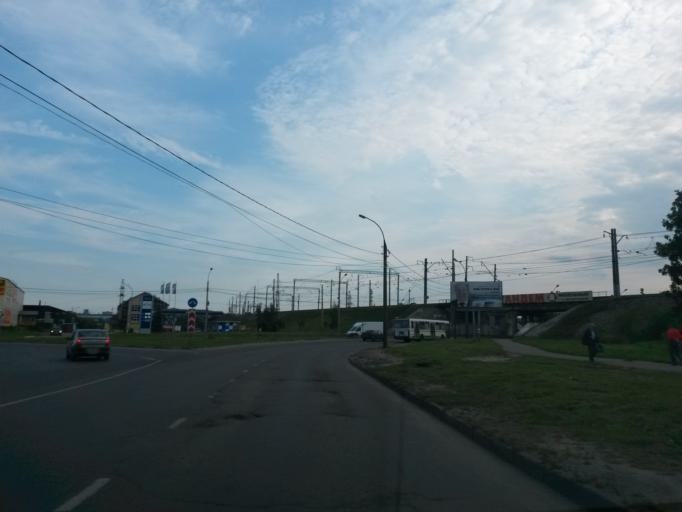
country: RU
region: Jaroslavl
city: Yaroslavl
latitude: 57.6190
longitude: 39.8483
